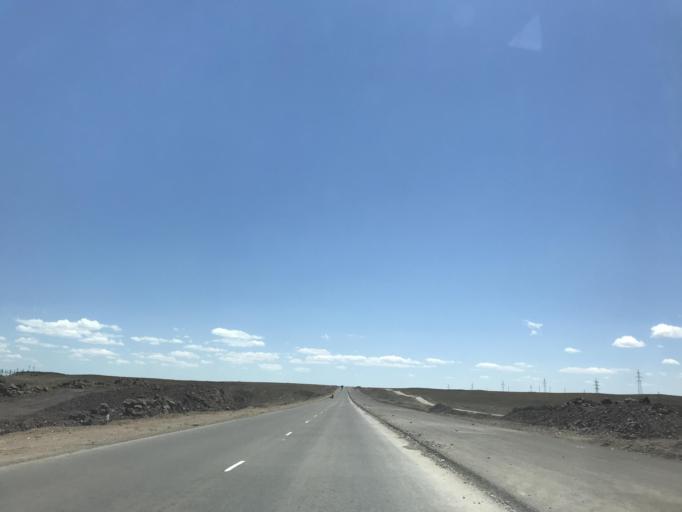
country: KZ
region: Zhambyl
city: Mynaral
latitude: 45.2746
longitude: 73.7851
